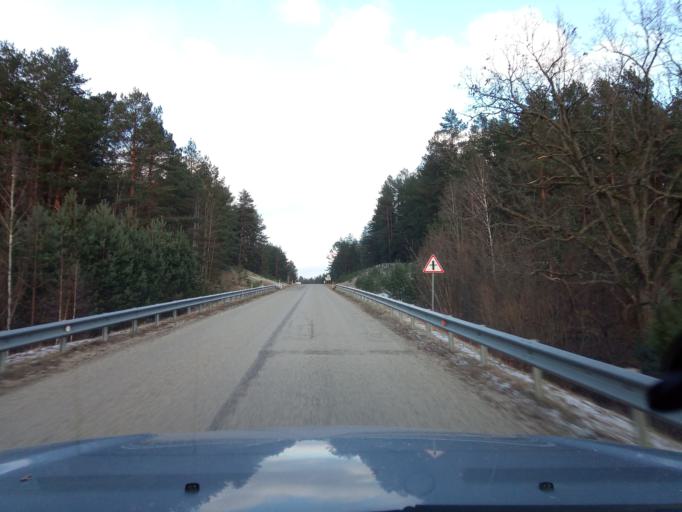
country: LT
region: Alytaus apskritis
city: Varena
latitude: 54.1306
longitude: 24.4628
